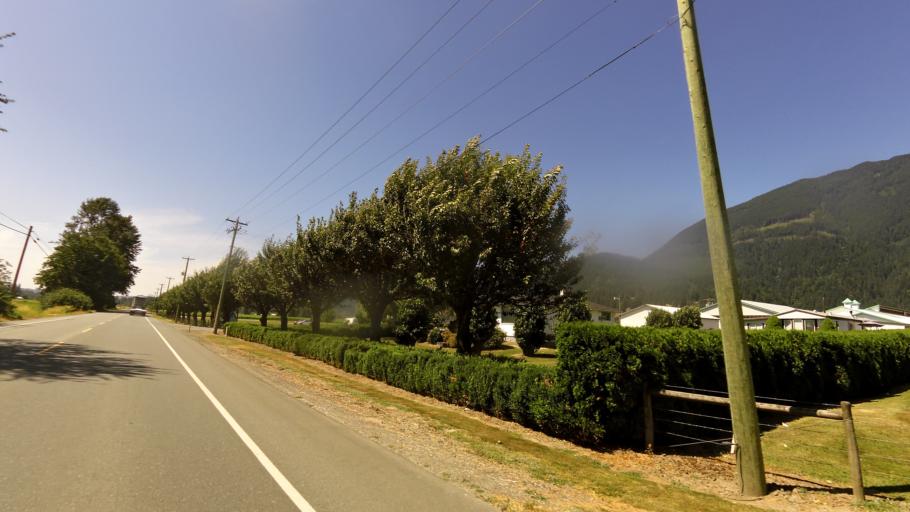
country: CA
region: British Columbia
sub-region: Fraser Valley Regional District
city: Chilliwack
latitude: 49.1693
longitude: -122.1101
